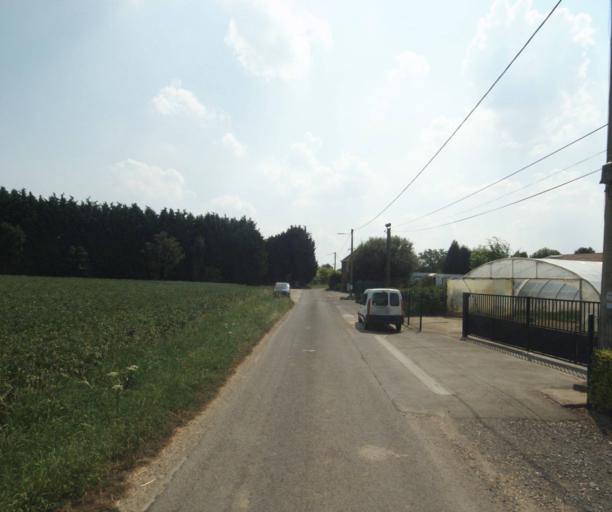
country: FR
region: Nord-Pas-de-Calais
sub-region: Departement du Nord
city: Linselles
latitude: 50.7237
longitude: 3.0407
